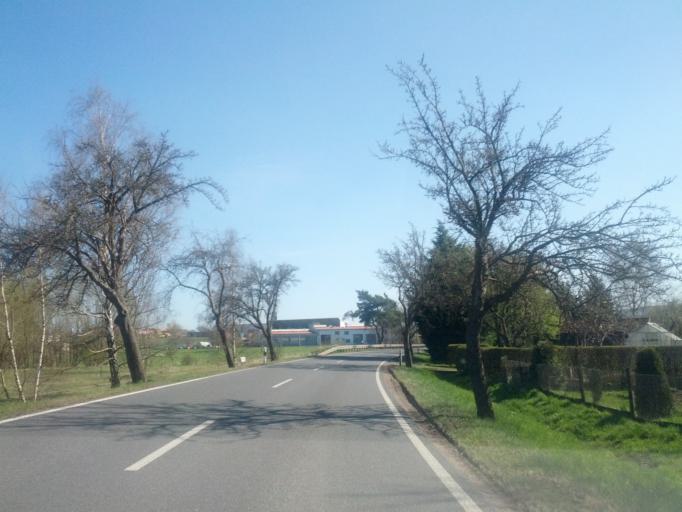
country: DE
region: Thuringia
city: Waltershausen
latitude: 50.9258
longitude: 10.5483
